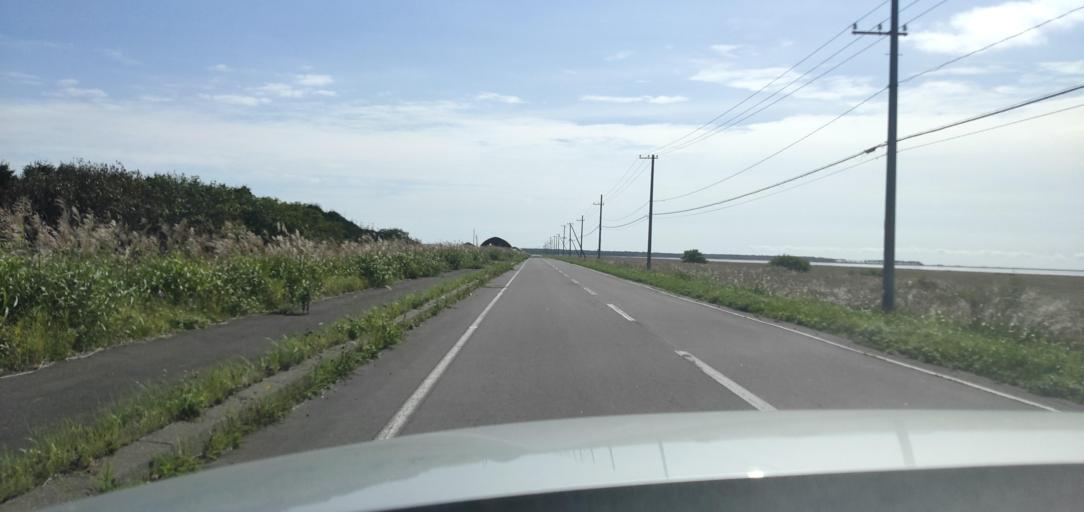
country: JP
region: Hokkaido
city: Shibetsu
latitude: 43.6188
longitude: 145.2314
